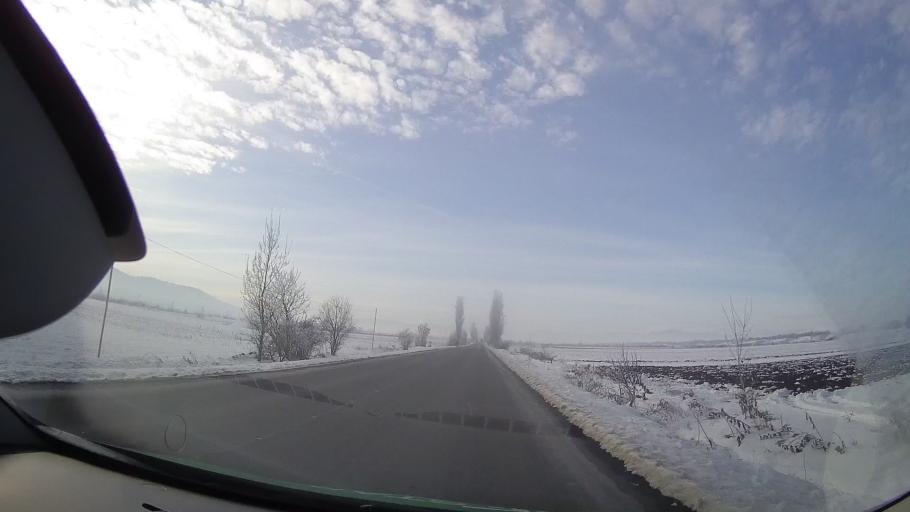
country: RO
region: Neamt
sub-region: Comuna Timisesti
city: Dumbrava
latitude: 47.2159
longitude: 26.4430
